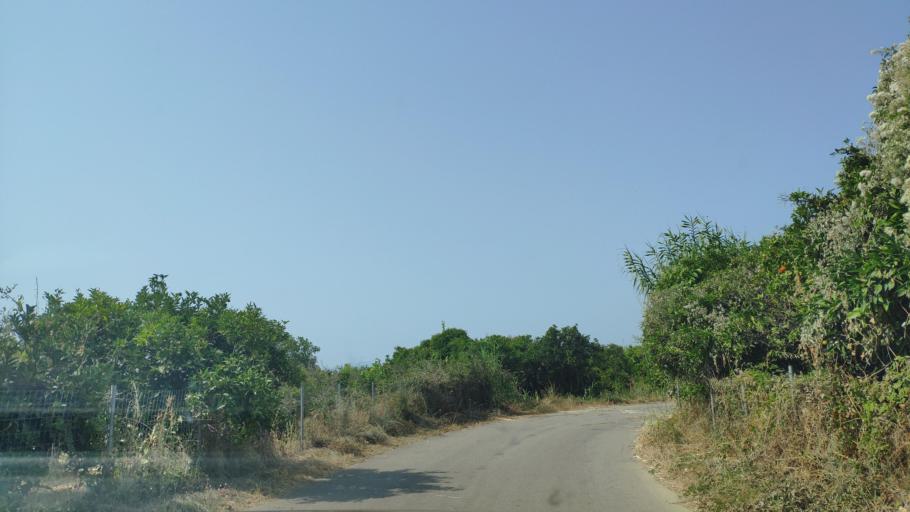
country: GR
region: Epirus
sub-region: Nomos Artas
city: Kompoti
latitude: 39.0764
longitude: 21.0835
